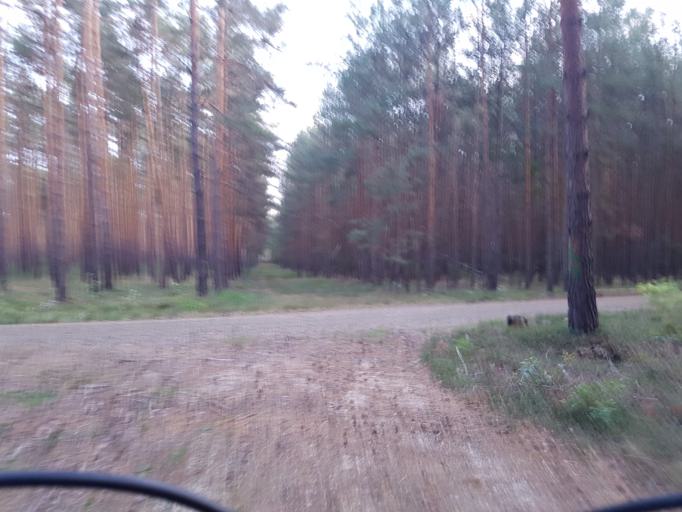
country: DE
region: Brandenburg
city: Trobitz
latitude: 51.5647
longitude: 13.4535
